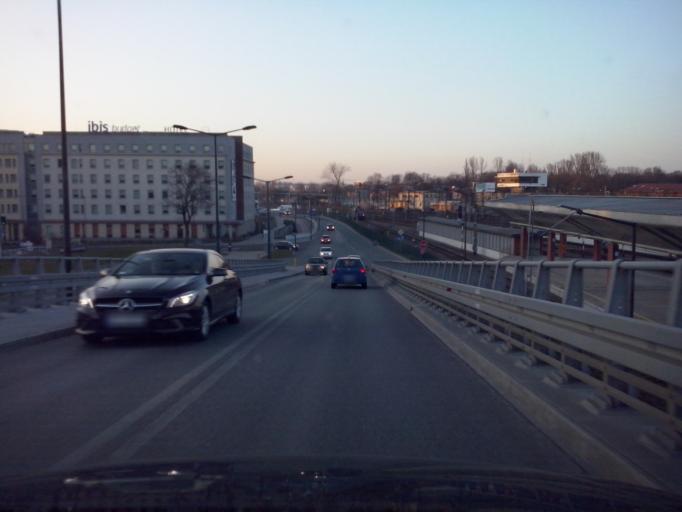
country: PL
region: Lesser Poland Voivodeship
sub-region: Krakow
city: Krakow
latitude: 50.0695
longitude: 19.9468
